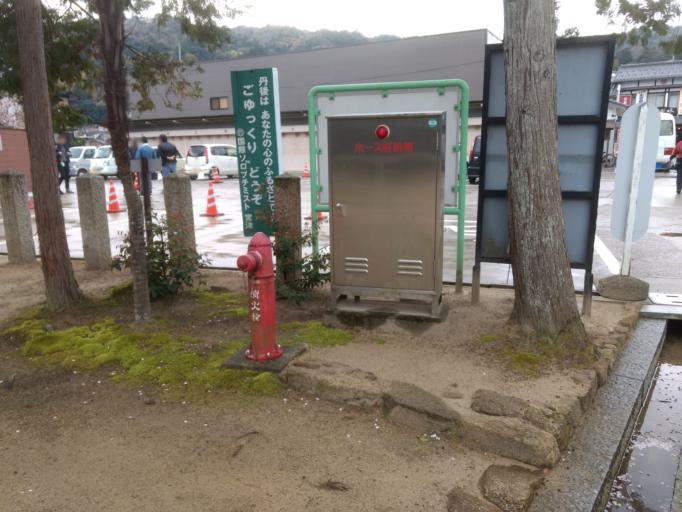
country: JP
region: Kyoto
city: Miyazu
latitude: 35.5584
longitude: 135.1840
